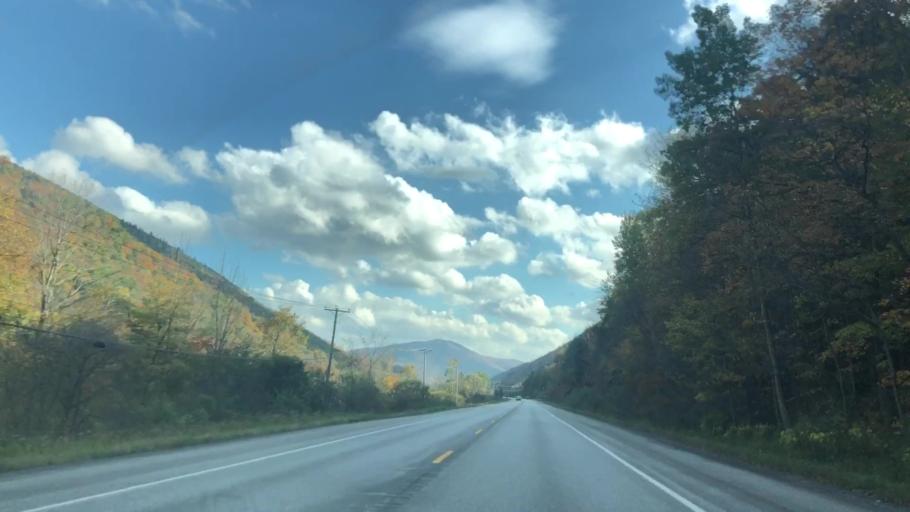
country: US
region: Vermont
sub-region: Rutland County
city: Rutland
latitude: 43.6464
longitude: -72.7694
